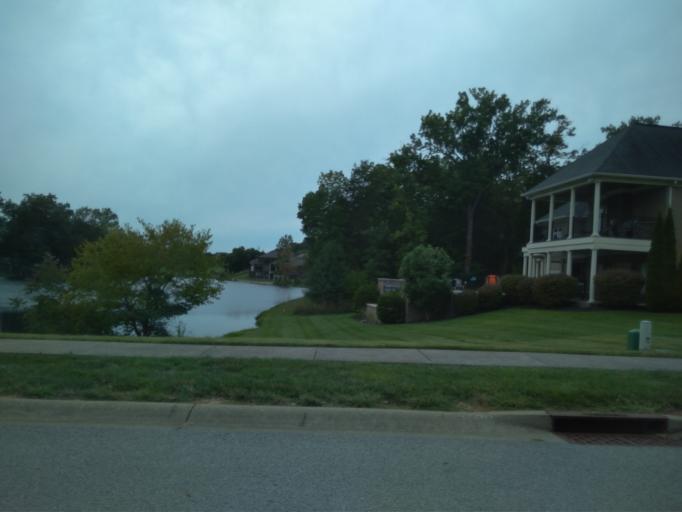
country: US
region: Kentucky
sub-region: Oldham County
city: Pewee Valley
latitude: 38.2777
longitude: -85.4760
